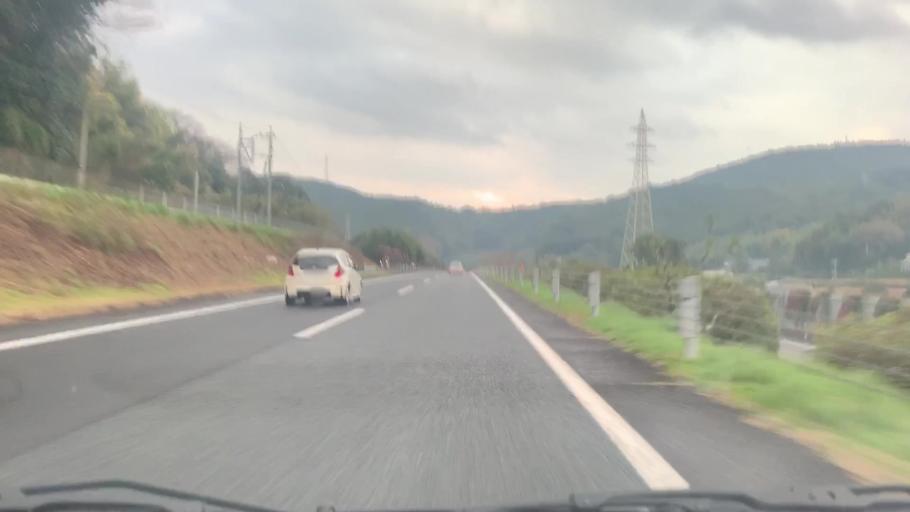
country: JP
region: Nagasaki
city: Omura
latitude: 32.8806
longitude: 129.9962
